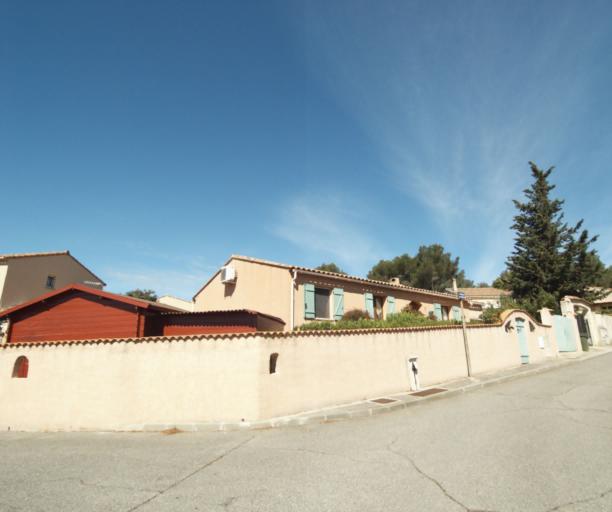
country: FR
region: Provence-Alpes-Cote d'Azur
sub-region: Departement des Bouches-du-Rhone
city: Rognac
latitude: 43.5116
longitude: 5.2099
